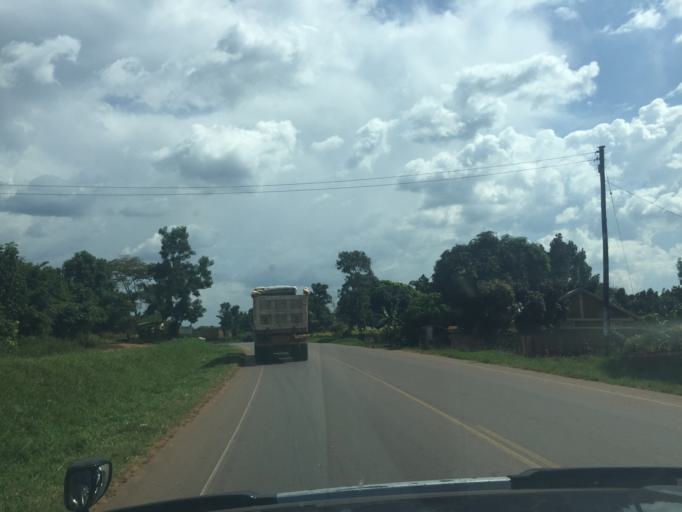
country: UG
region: Central Region
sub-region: Luwero District
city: Wobulenzi
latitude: 0.7416
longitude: 32.5169
